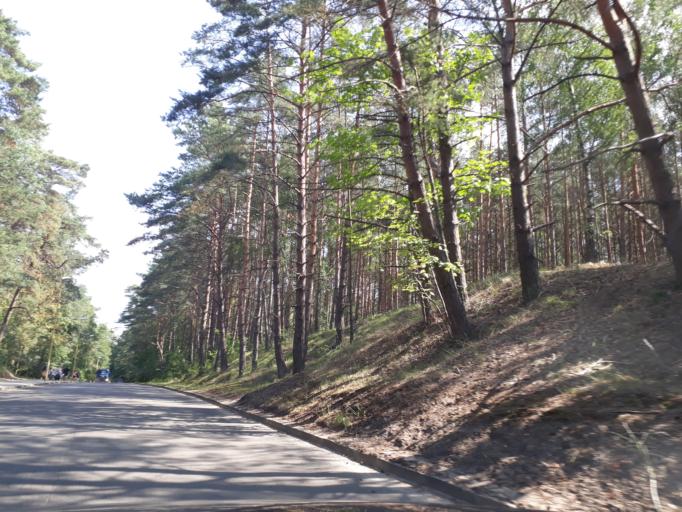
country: PL
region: West Pomeranian Voivodeship
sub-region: Swinoujscie
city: Swinoujscie
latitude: 53.9226
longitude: 14.2257
